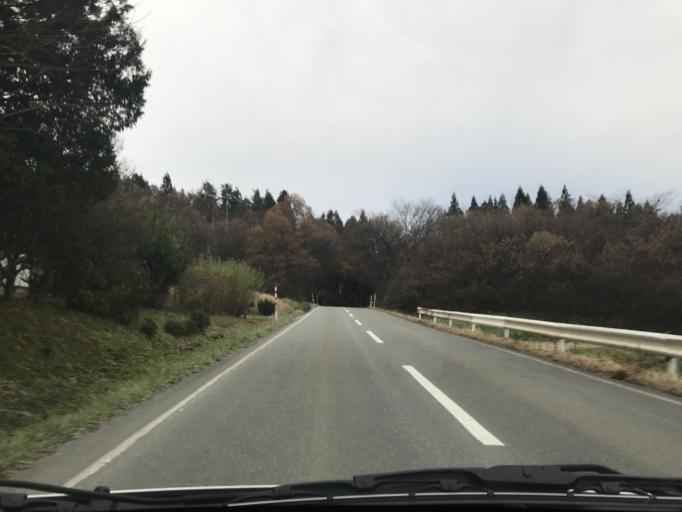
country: JP
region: Iwate
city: Kitakami
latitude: 39.2524
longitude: 141.2679
